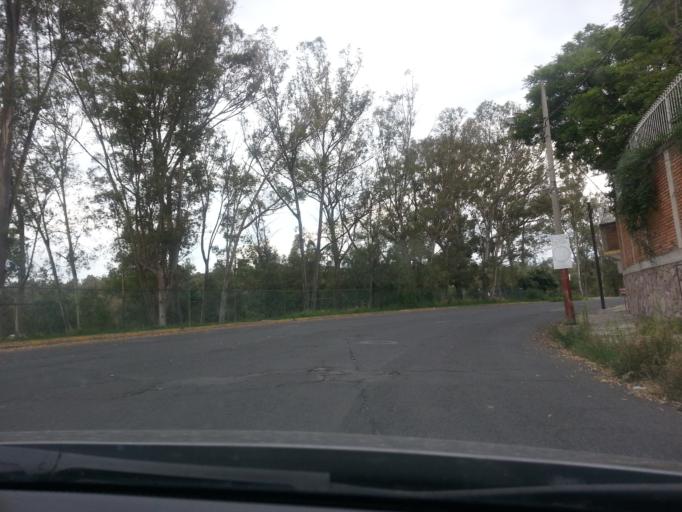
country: MX
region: Mexico
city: Cuautitlan Izcalli
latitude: 19.6211
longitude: -99.2459
